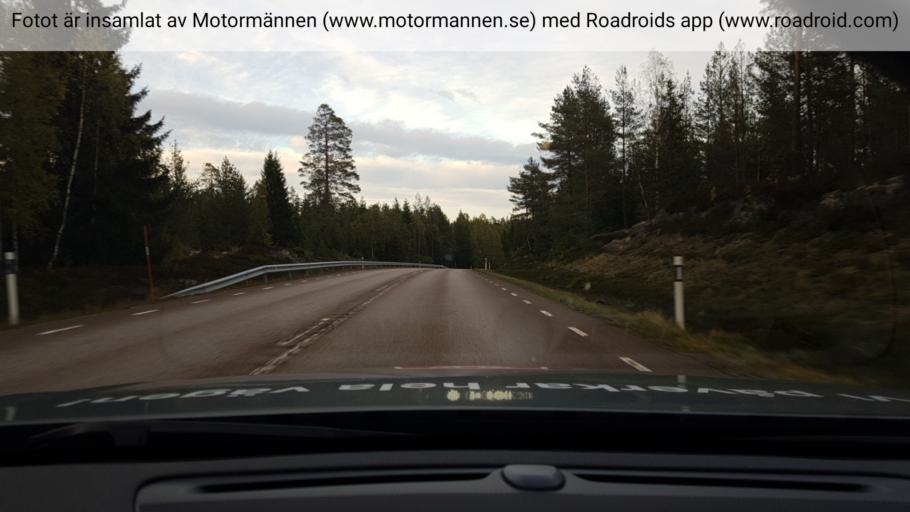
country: SE
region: Vaestra Goetaland
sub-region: Amals Kommun
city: Amal
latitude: 59.0731
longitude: 12.5654
